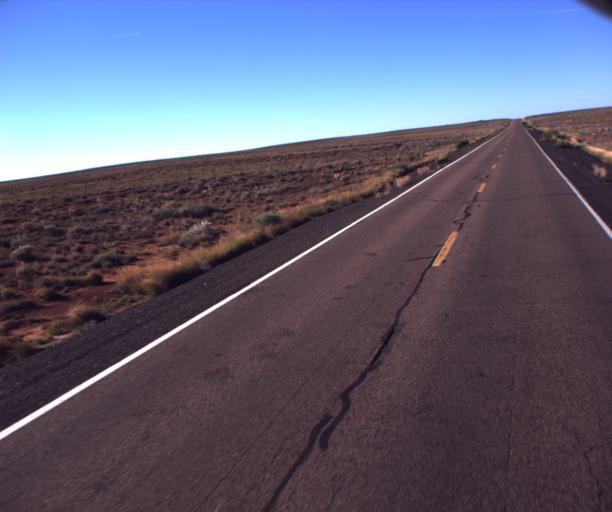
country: US
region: Arizona
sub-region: Navajo County
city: Holbrook
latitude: 34.8435
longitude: -110.1790
